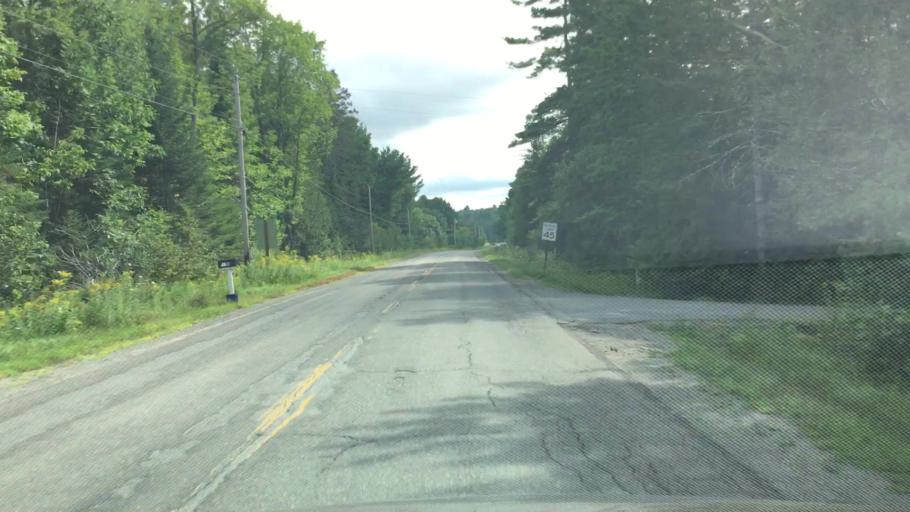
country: US
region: Maine
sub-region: Penobscot County
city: Hampden
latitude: 44.7218
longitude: -68.8663
